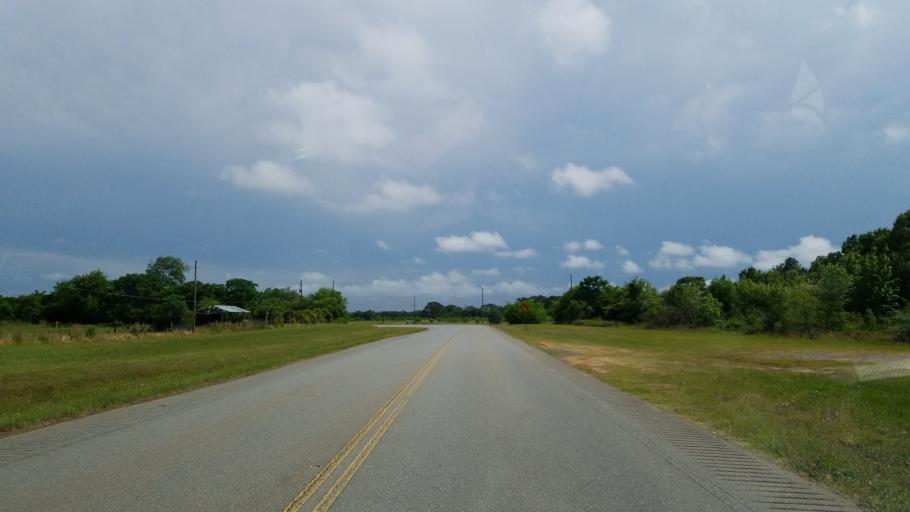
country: US
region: Georgia
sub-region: Houston County
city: Perry
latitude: 32.4406
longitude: -83.7792
